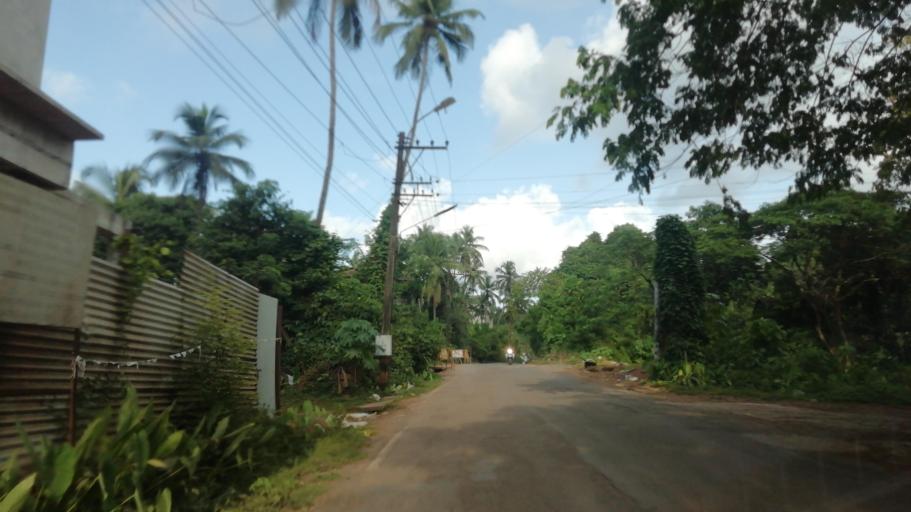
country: IN
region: Goa
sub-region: North Goa
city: Queula
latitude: 15.3911
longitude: 73.9968
